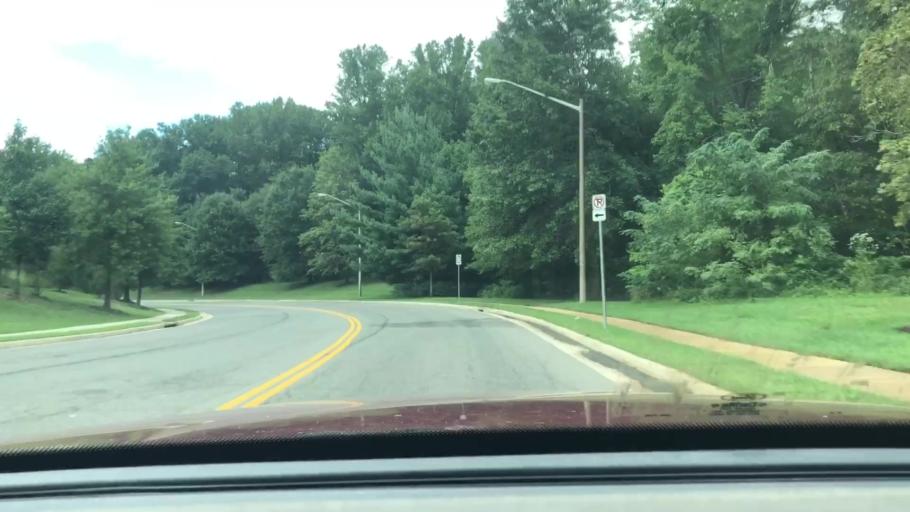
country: US
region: Virginia
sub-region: Fairfax County
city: Springfield
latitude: 38.7655
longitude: -77.1964
